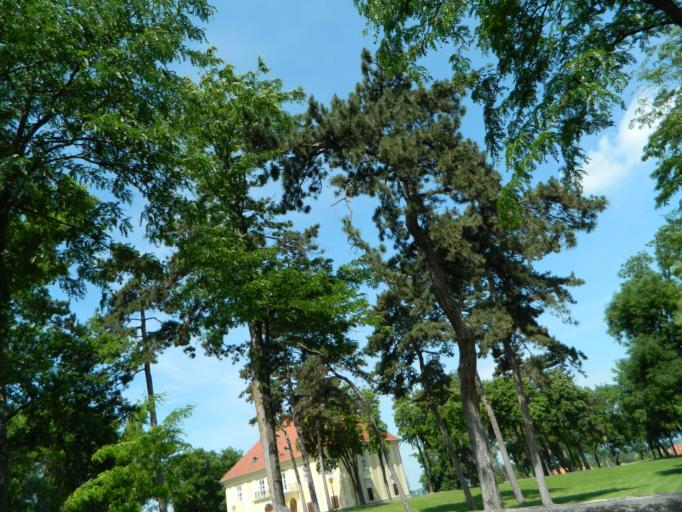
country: HU
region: Somogy
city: Balatonfoldvar
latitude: 46.8258
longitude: 17.9028
